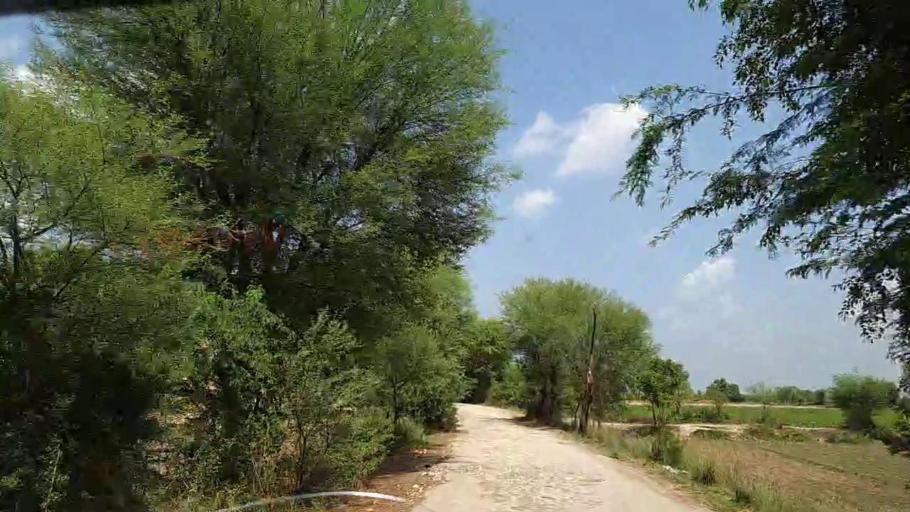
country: PK
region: Sindh
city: Tharu Shah
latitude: 26.9991
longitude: 68.0646
